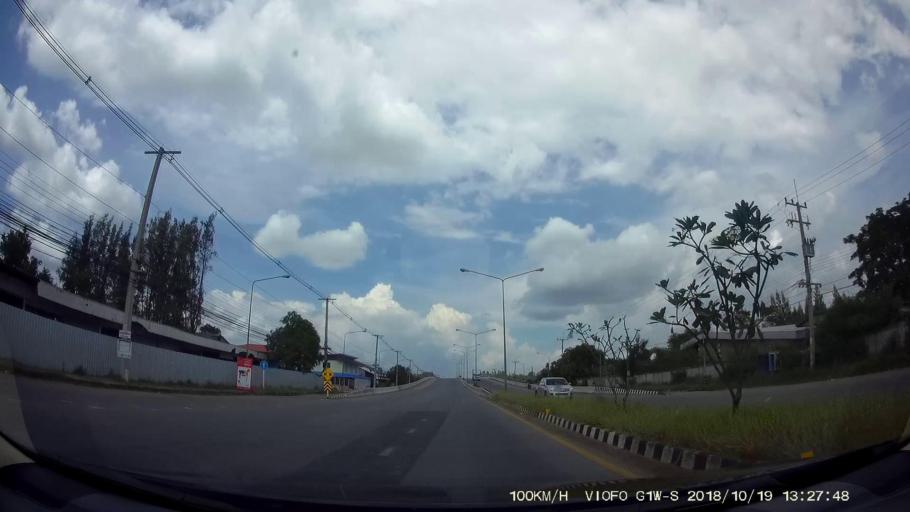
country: TH
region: Chaiyaphum
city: Chatturat
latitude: 15.5532
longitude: 101.8437
